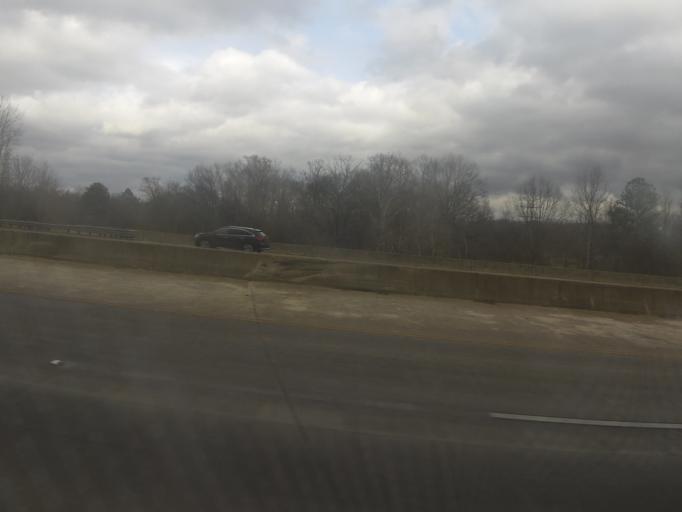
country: US
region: Georgia
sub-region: Catoosa County
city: Indian Springs
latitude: 34.9552
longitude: -85.1795
